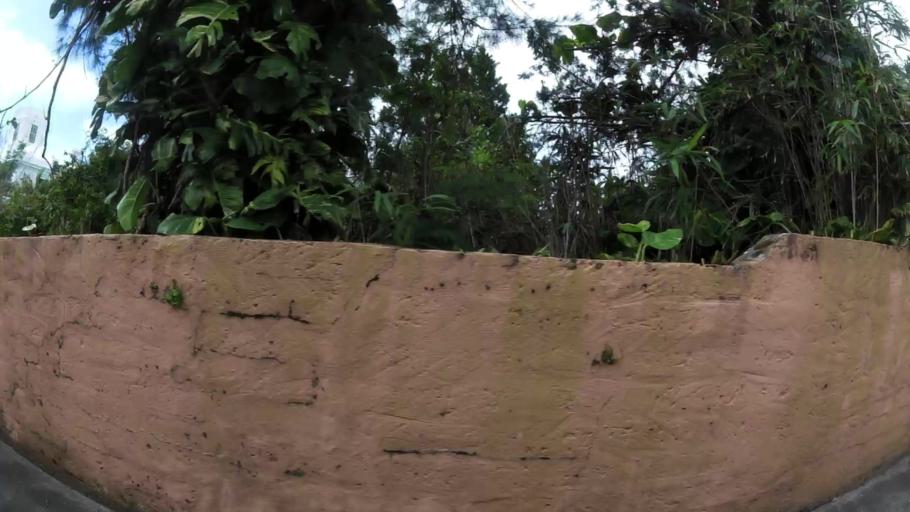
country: BM
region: Saint George
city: Saint George
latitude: 32.3817
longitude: -64.6713
